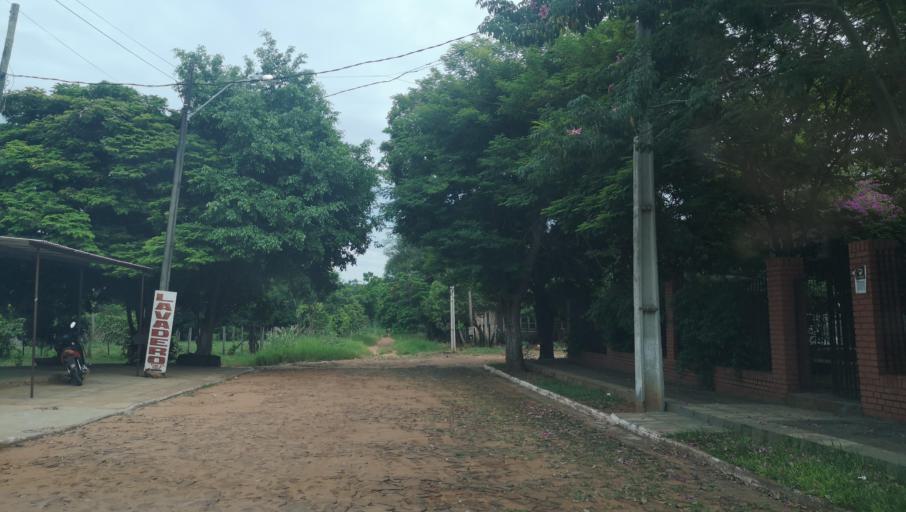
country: PY
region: San Pedro
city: Capiibary
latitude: -24.7291
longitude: -56.0204
